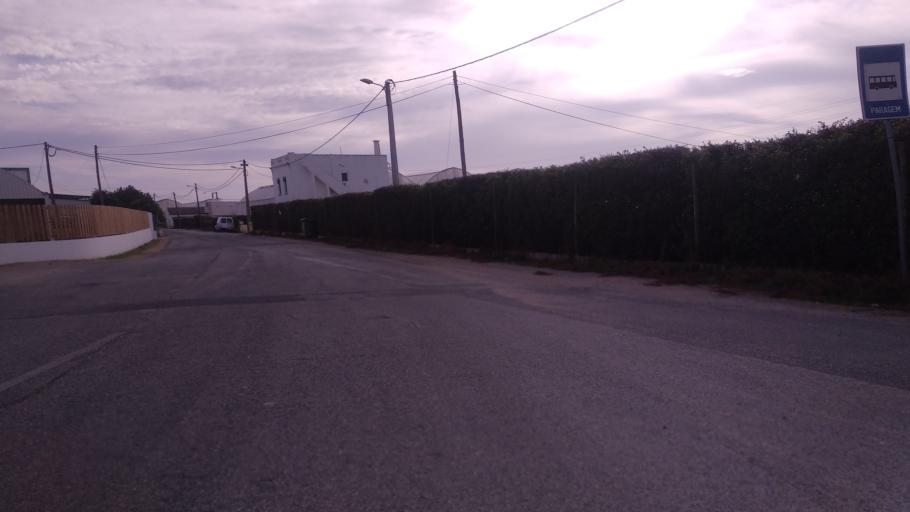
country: PT
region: Faro
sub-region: Faro
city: Faro
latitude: 37.0404
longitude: -7.9393
